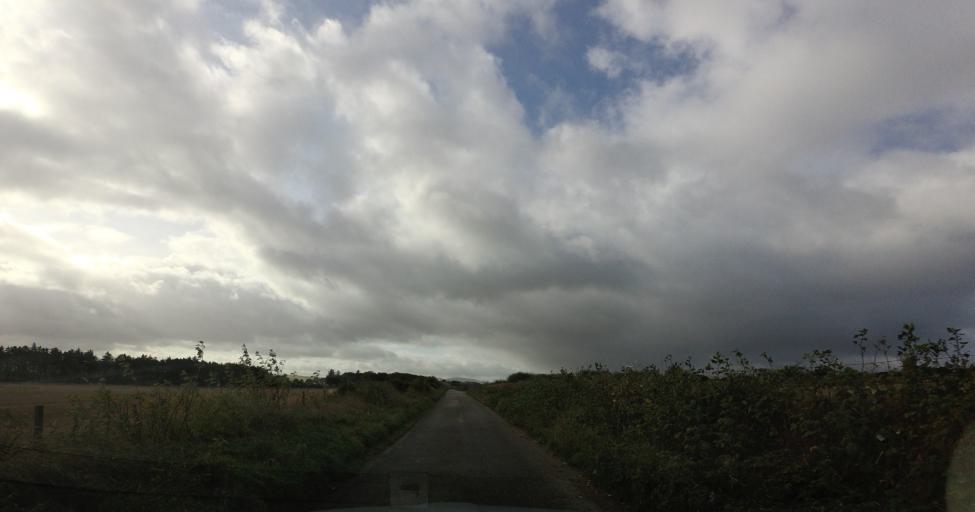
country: GB
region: Scotland
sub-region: Aberdeenshire
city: Whitehills
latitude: 57.6677
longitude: -2.5943
